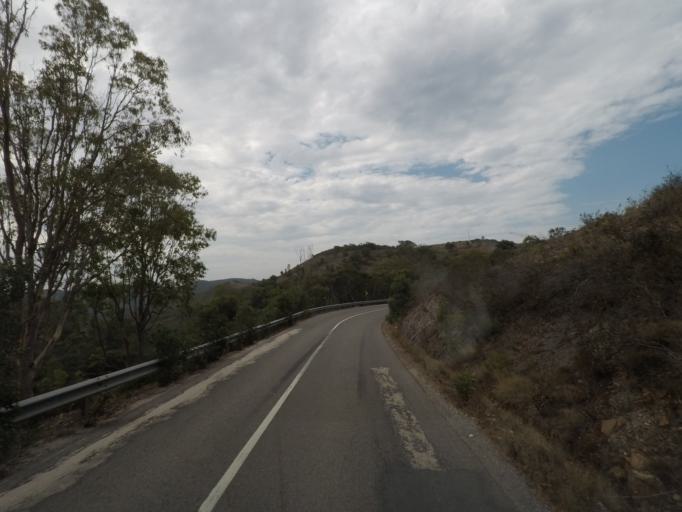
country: PT
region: Faro
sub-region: Aljezur
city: Aljezur
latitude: 37.2115
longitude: -8.8379
